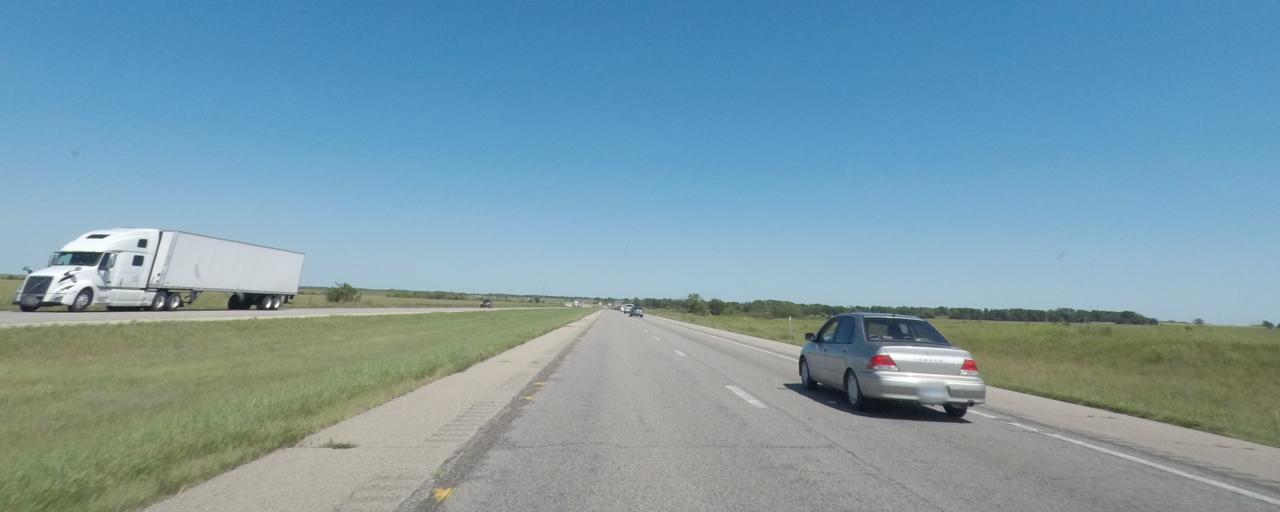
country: US
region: Kansas
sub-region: Lyon County
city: Emporia
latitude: 38.4130
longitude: -95.9413
